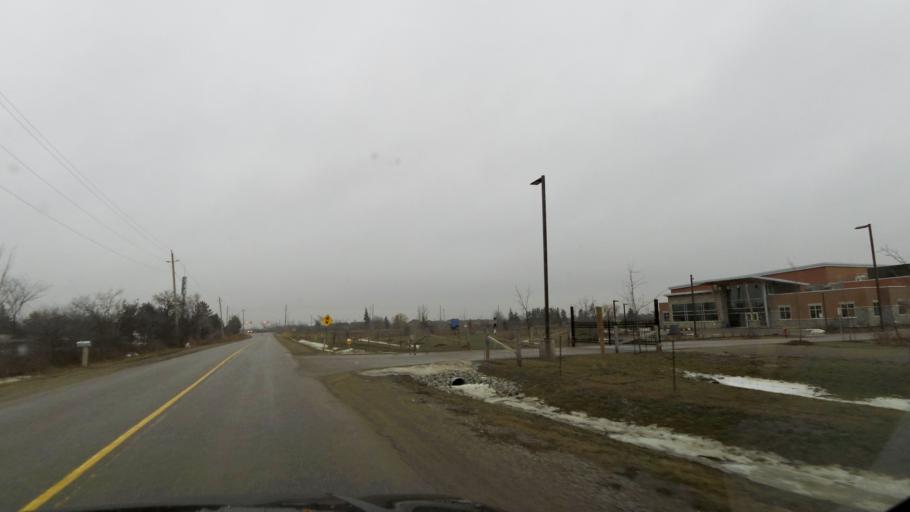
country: CA
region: Ontario
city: Brampton
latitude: 43.8023
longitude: -79.7514
